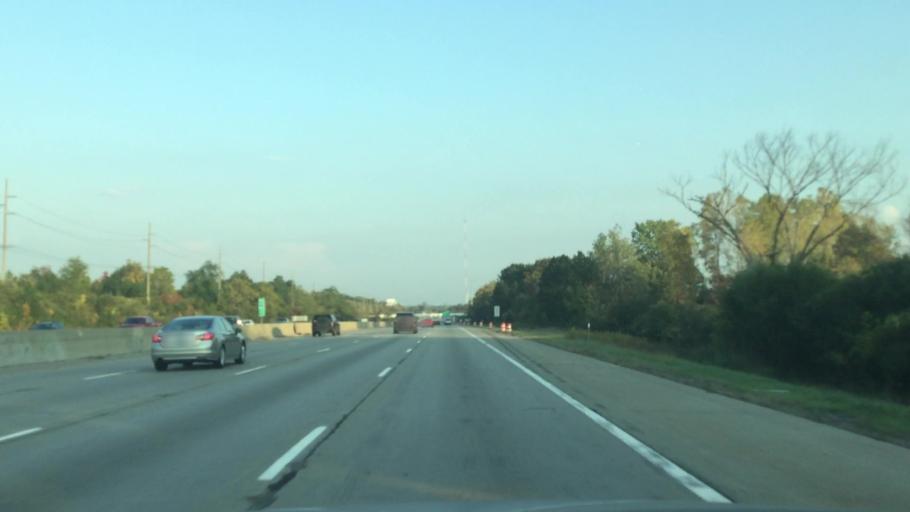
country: US
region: Michigan
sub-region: Oakland County
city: Farmington Hills
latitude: 42.4953
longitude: -83.3469
